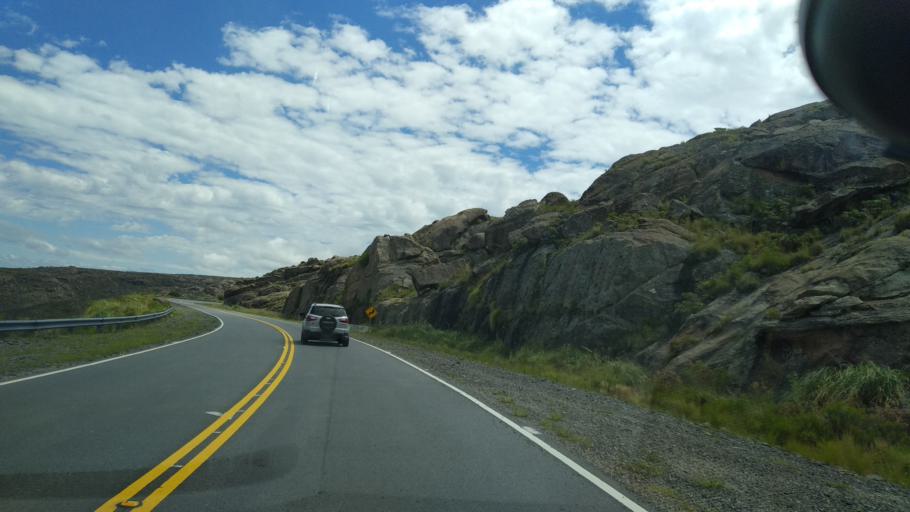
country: AR
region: Cordoba
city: Mina Clavero
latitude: -31.7531
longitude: -64.9108
